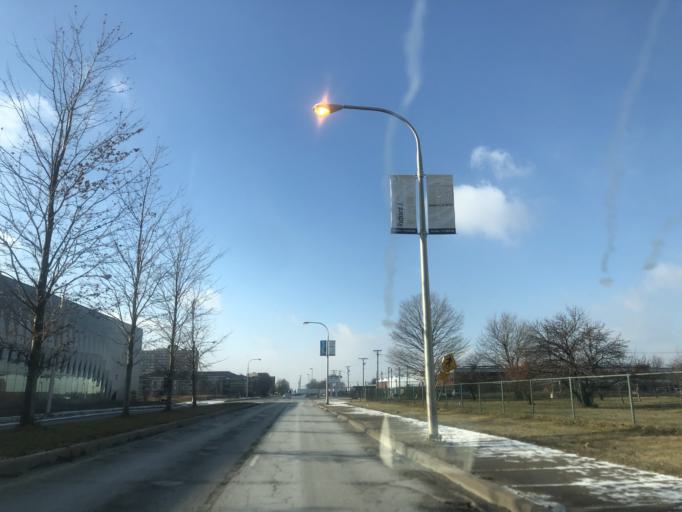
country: US
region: Illinois
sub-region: Cook County
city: Hometown
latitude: 41.7551
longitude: -87.7244
